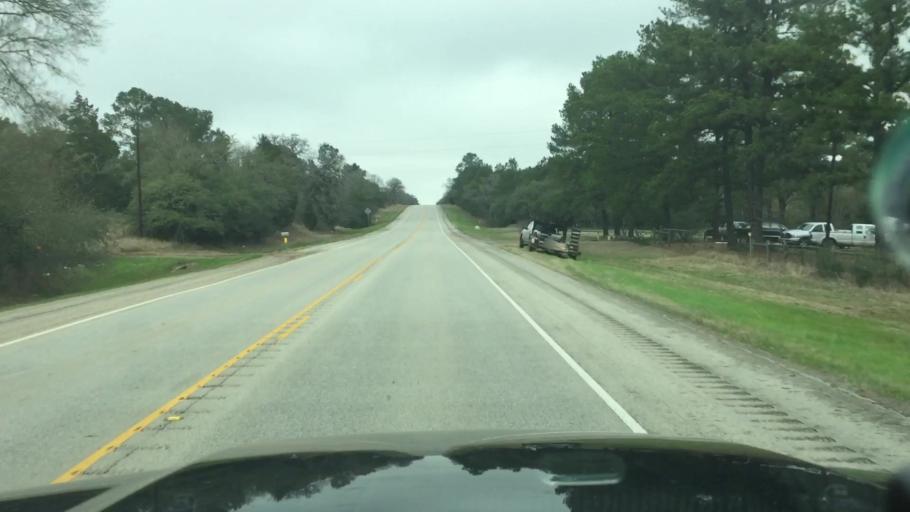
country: US
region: Texas
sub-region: Lee County
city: Giddings
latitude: 30.0693
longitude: -96.9166
